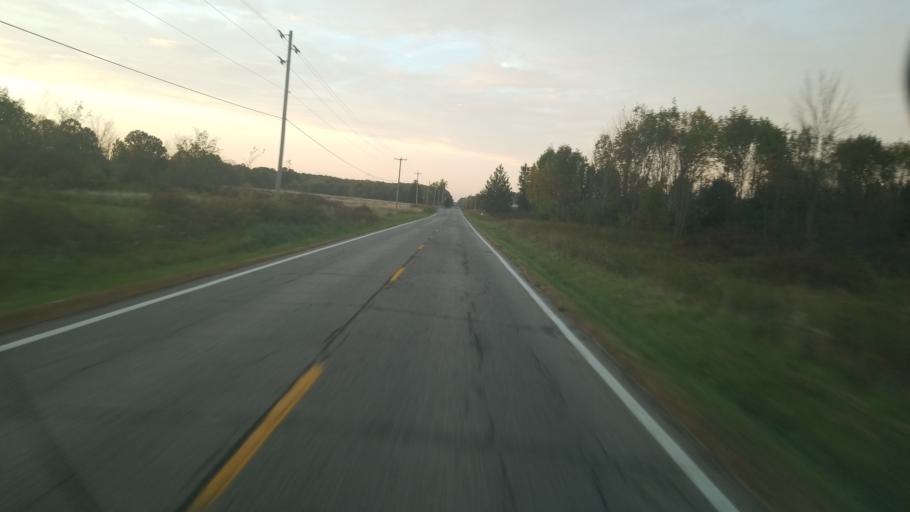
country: US
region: Ohio
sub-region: Ashtabula County
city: Andover
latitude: 41.6391
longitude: -80.6669
